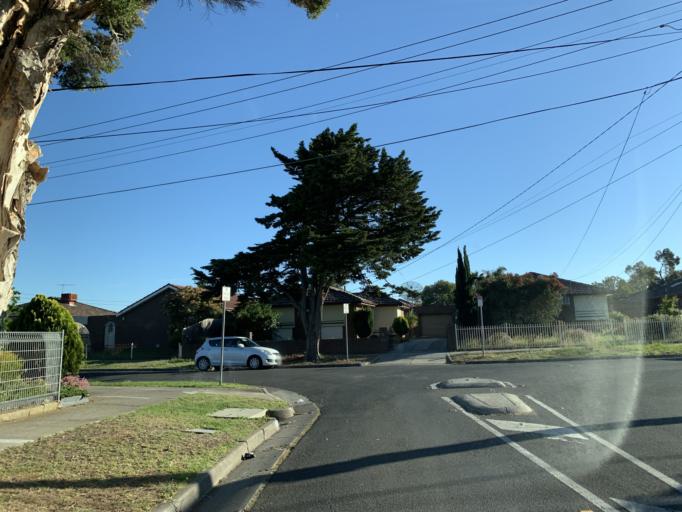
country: AU
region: Victoria
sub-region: Brimbank
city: Sunshine North
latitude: -37.7589
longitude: 144.8142
